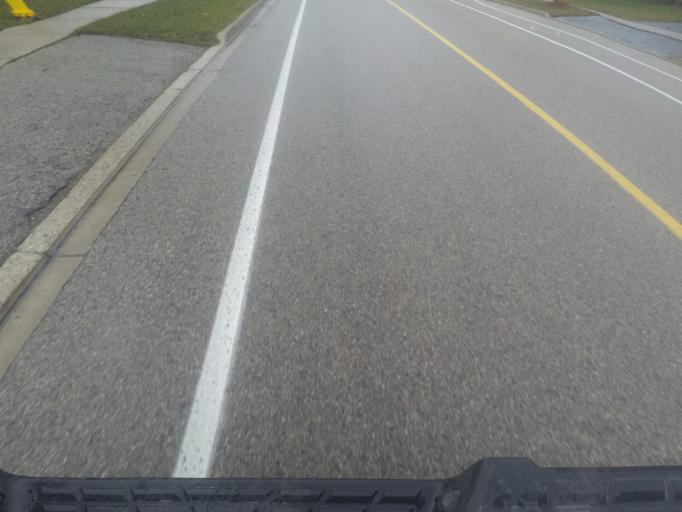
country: CN
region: Xinjiang Uygur Zizhiqu
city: Ayxin Siri
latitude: 43.4929
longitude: 80.5810
